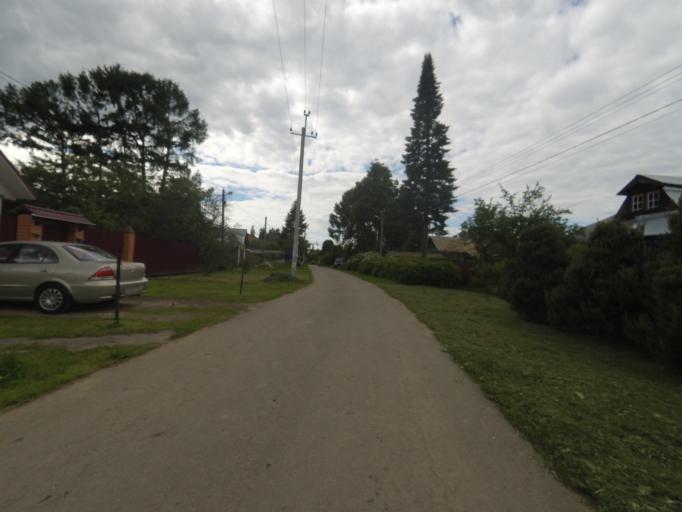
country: RU
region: Moskovskaya
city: Marfino
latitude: 56.0554
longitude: 37.6416
